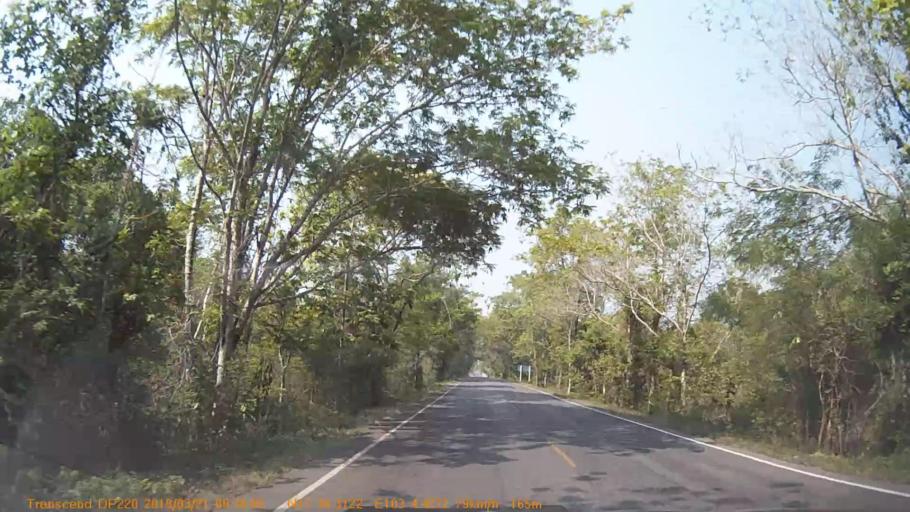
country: TH
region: Changwat Udon Thani
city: Phibun Rak
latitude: 17.6050
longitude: 103.0735
